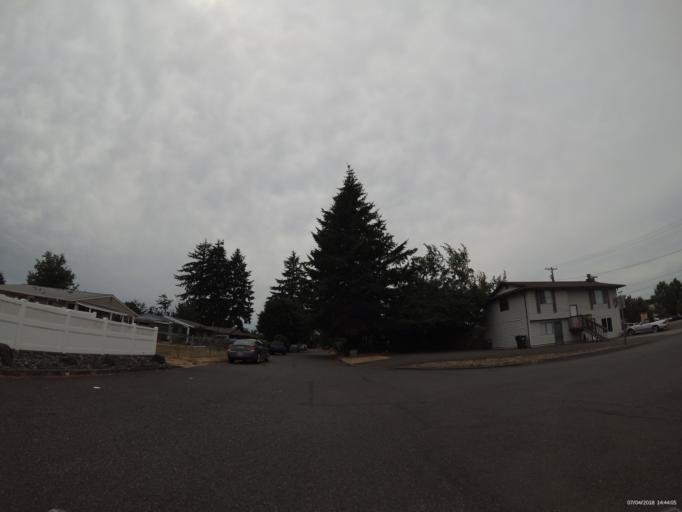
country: US
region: Washington
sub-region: Pierce County
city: Lakewood
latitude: 47.1662
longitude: -122.5037
